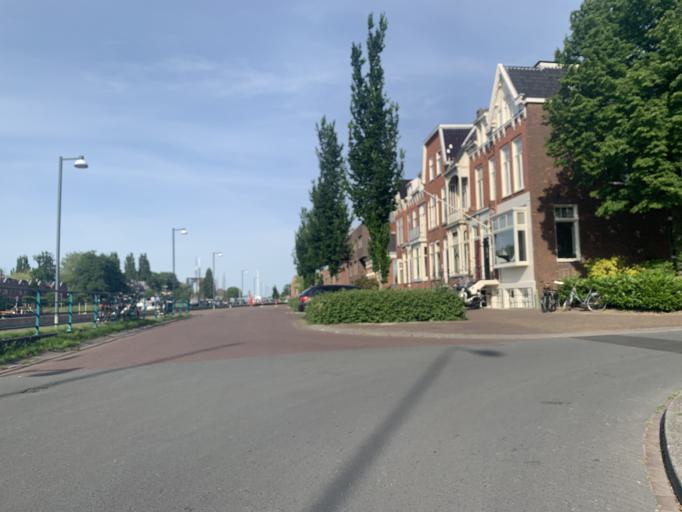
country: NL
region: Groningen
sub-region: Gemeente Groningen
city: Oosterpark
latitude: 53.2170
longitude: 6.5807
